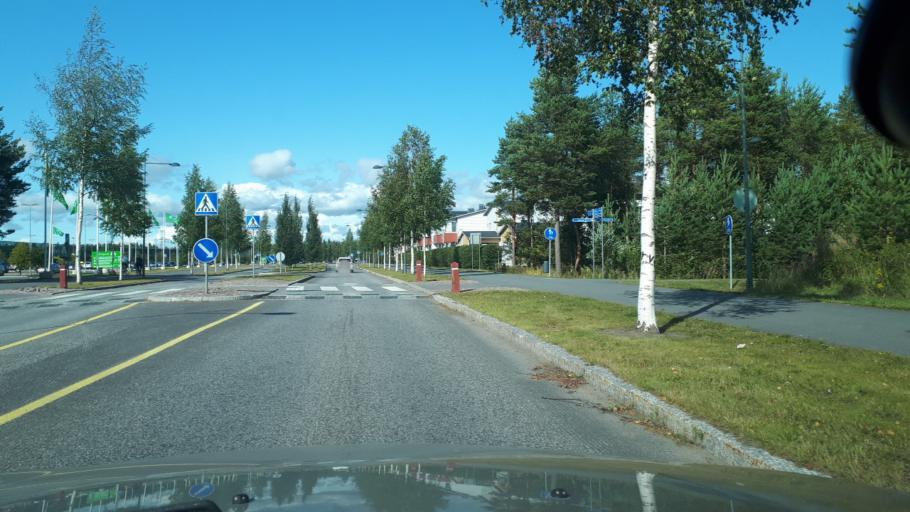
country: FI
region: Northern Ostrobothnia
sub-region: Oulu
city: Oulu
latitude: 65.0738
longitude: 25.4475
